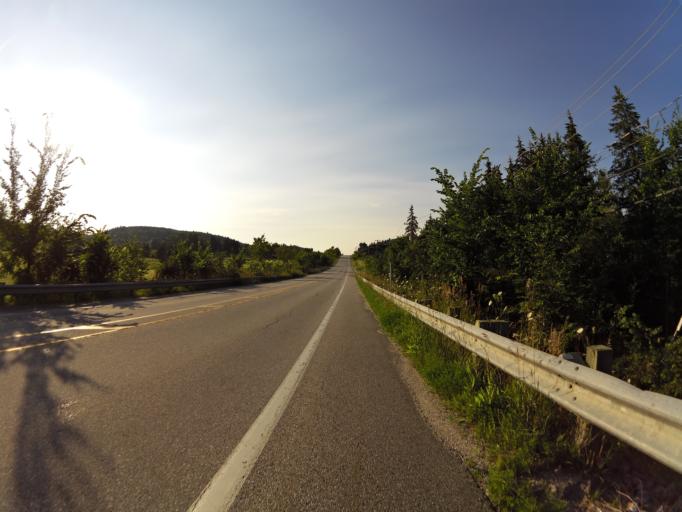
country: CA
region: Quebec
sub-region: Outaouais
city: Wakefield
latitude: 45.6015
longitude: -75.9026
